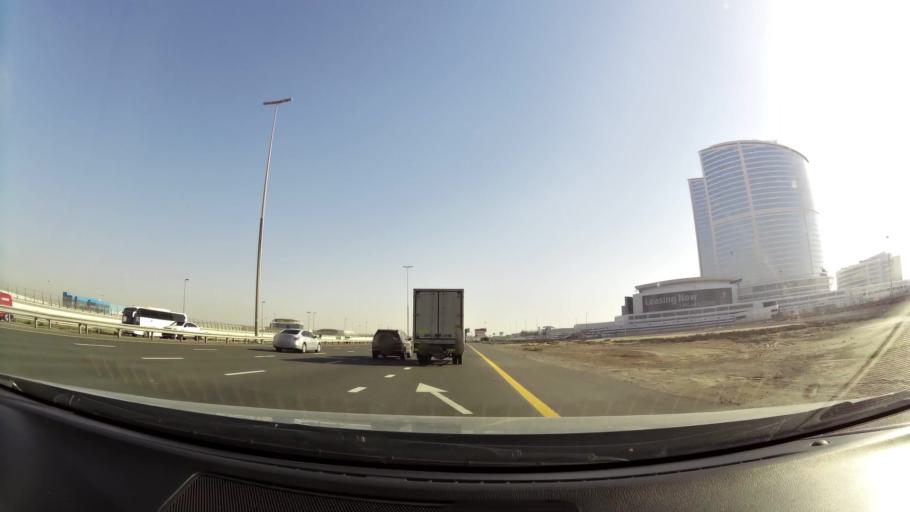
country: AE
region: Dubai
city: Dubai
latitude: 24.9660
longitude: 55.0838
